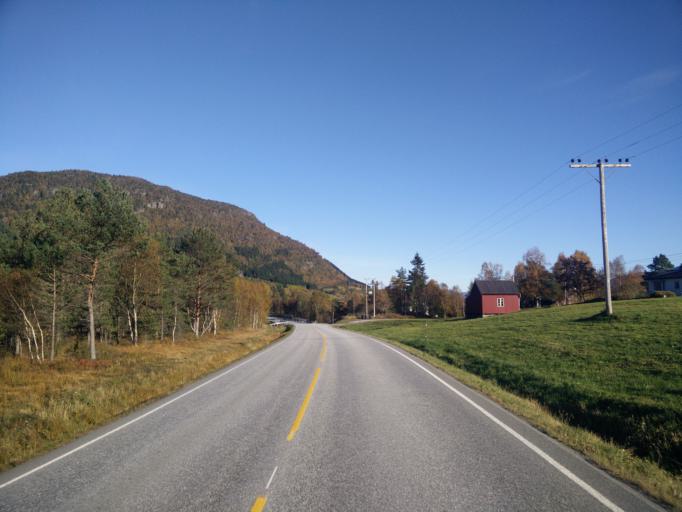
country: NO
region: More og Romsdal
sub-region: Tingvoll
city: Tingvoll
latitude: 63.0454
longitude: 8.0694
